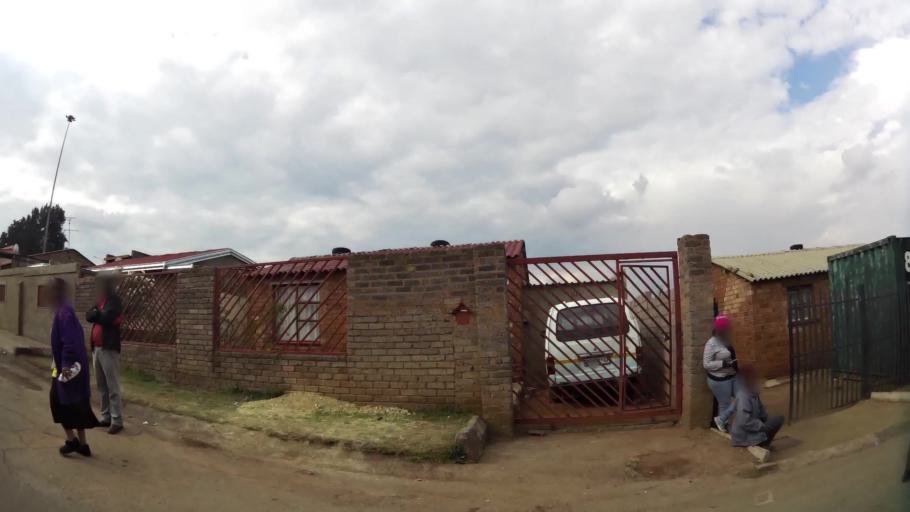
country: ZA
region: Gauteng
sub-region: City of Johannesburg Metropolitan Municipality
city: Soweto
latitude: -26.2353
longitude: 27.8671
